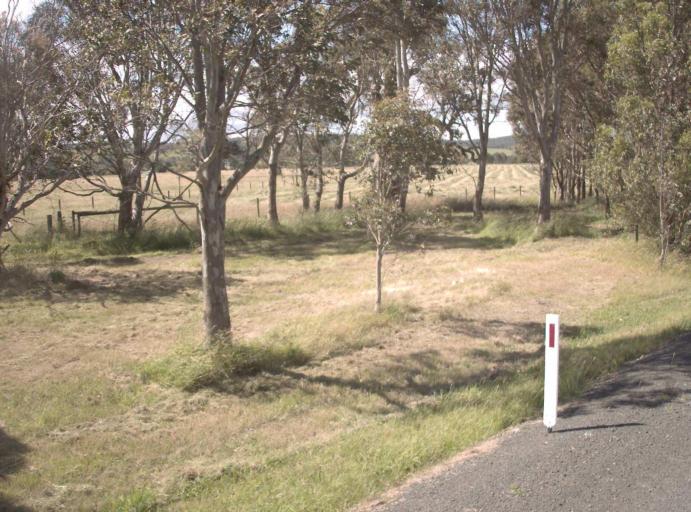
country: AU
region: Victoria
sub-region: Latrobe
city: Traralgon
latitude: -38.1416
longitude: 146.5286
